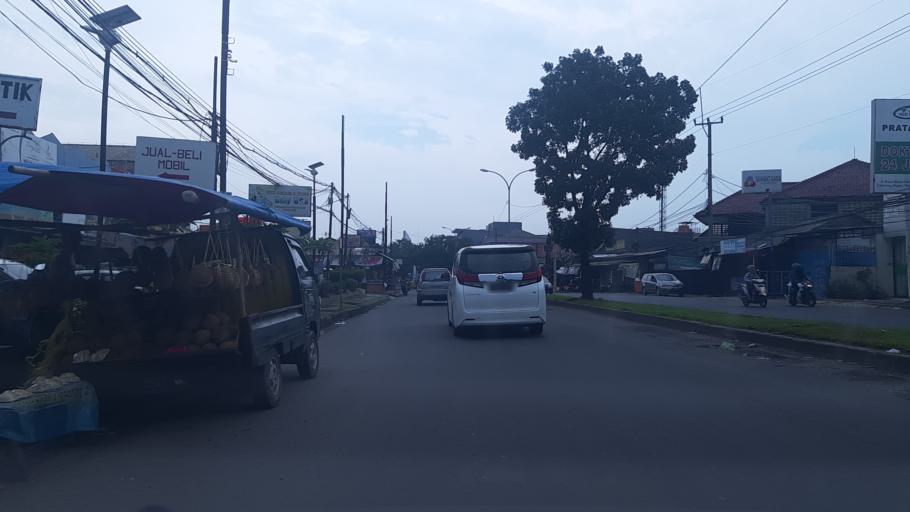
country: ID
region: West Java
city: Cibinong
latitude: -6.4762
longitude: 106.8635
